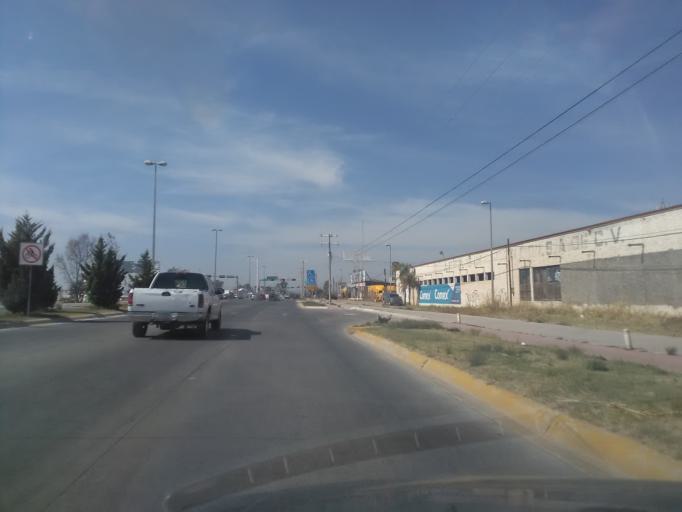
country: MX
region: Durango
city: Victoria de Durango
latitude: 24.0768
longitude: -104.5912
